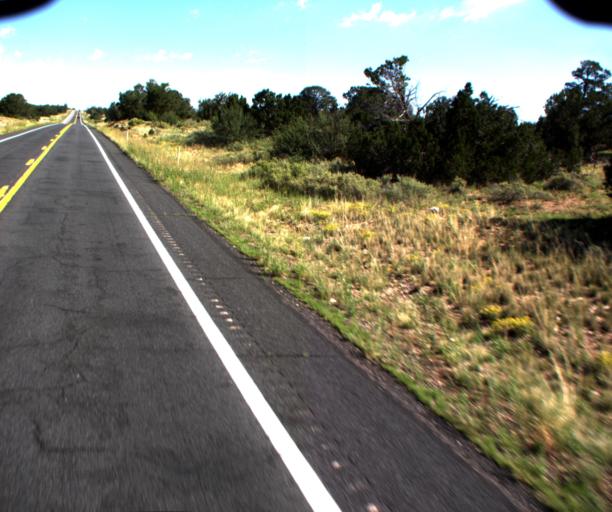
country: US
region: Arizona
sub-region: Coconino County
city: Grand Canyon Village
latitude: 35.8092
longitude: -112.1313
